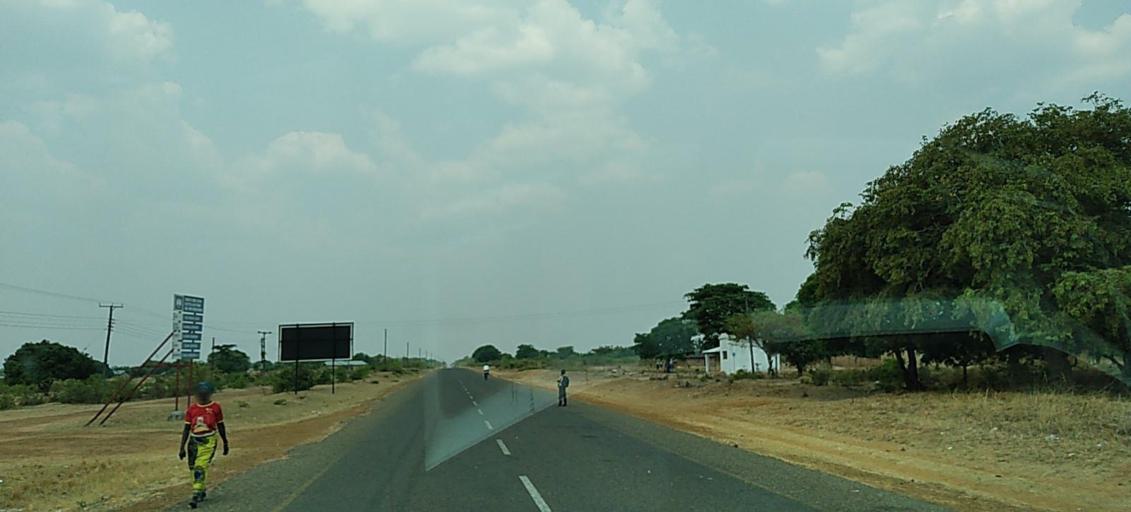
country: ZM
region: North-Western
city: Zambezi
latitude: -13.5509
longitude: 23.1232
